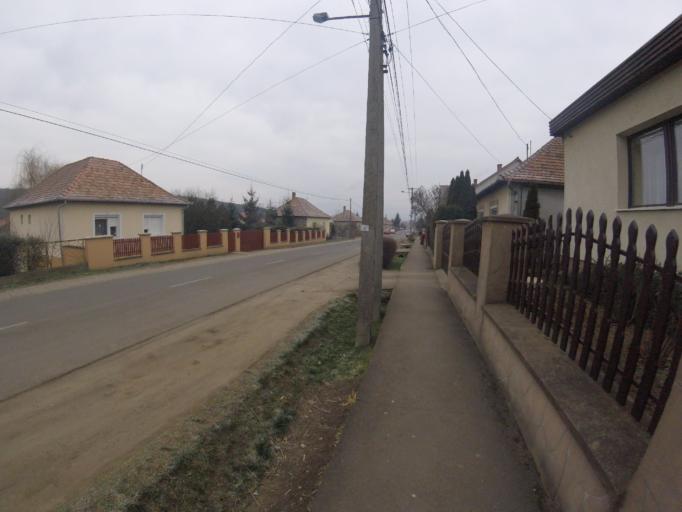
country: HU
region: Nograd
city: Paszto
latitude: 47.9532
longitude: 19.6911
